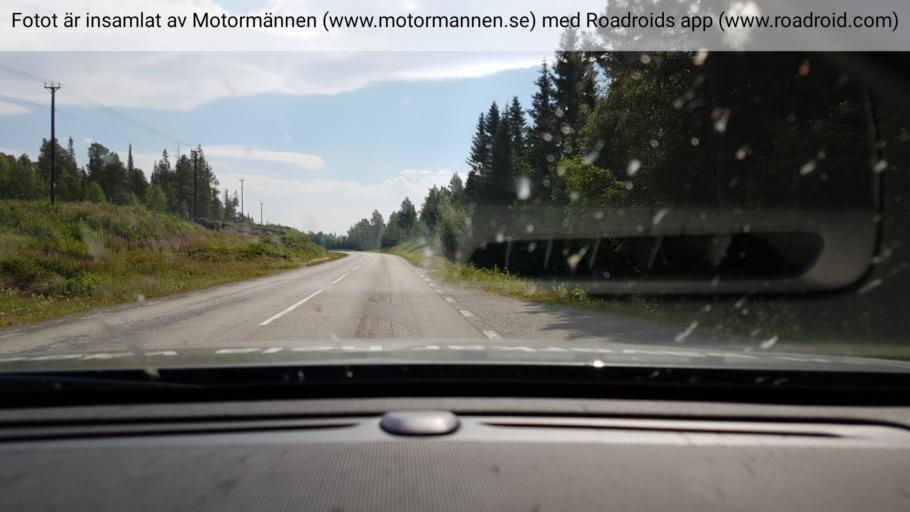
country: SE
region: Vaesterbotten
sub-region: Vilhelmina Kommun
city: Sjoberg
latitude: 65.5398
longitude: 15.5865
